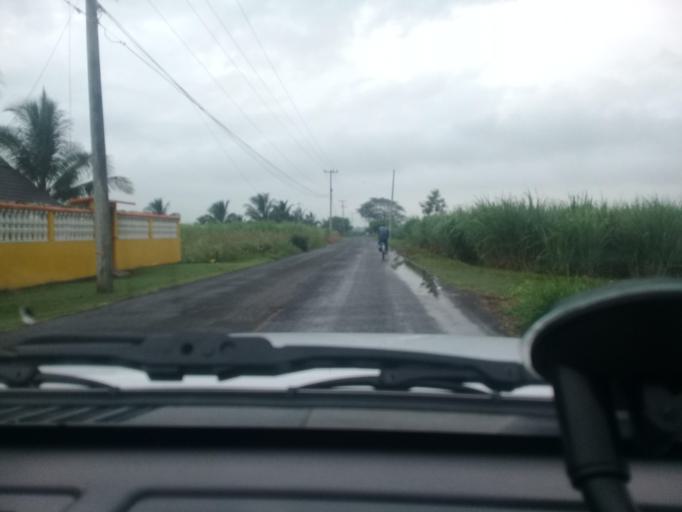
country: MX
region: Veracruz
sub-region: La Antigua
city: Nicolas Blanco (San Pancho)
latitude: 19.3528
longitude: -96.3459
